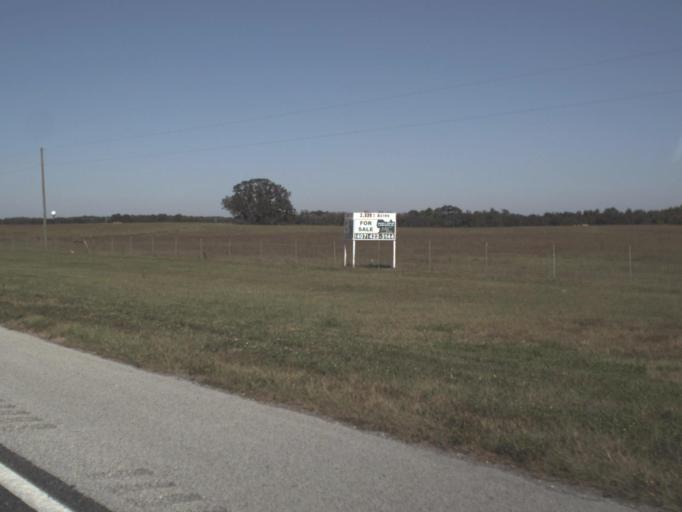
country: US
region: Florida
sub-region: Sumter County
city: Wildwood
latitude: 28.7855
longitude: -81.9783
